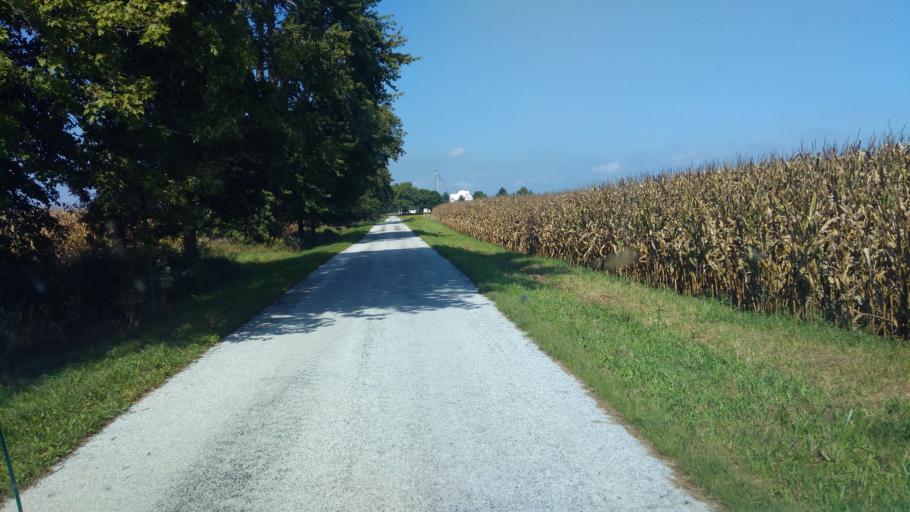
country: US
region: Ohio
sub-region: Hardin County
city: Kenton
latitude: 40.6761
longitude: -83.6093
